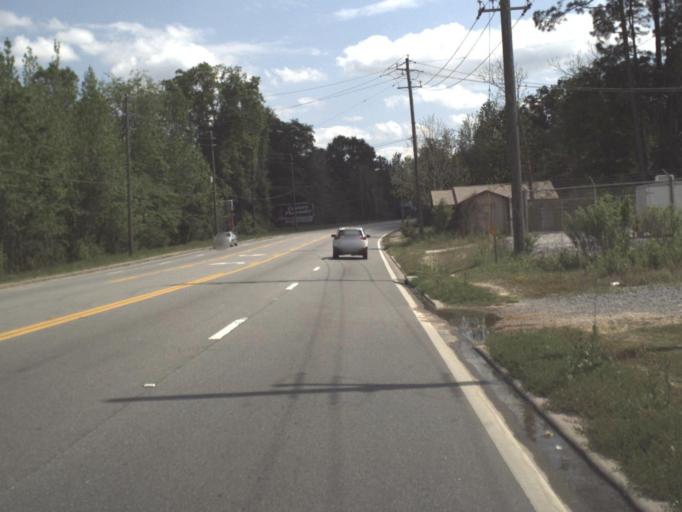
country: US
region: Alabama
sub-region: Escambia County
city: Flomaton
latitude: 30.9878
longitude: -87.2567
